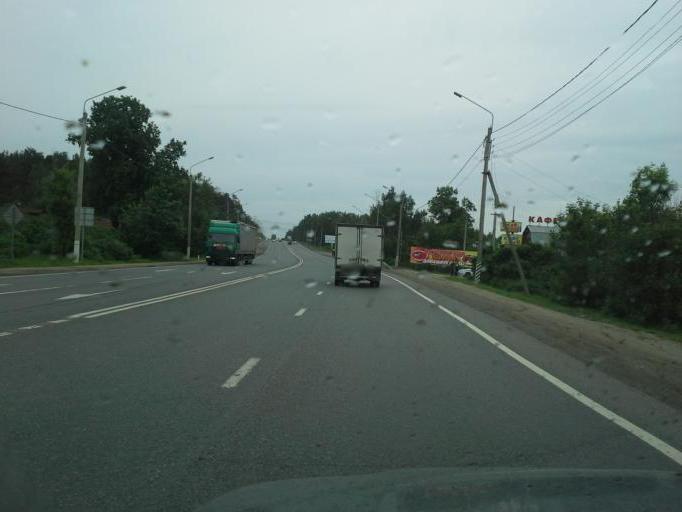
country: RU
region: Vladimir
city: Pokrov
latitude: 55.9005
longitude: 39.0739
